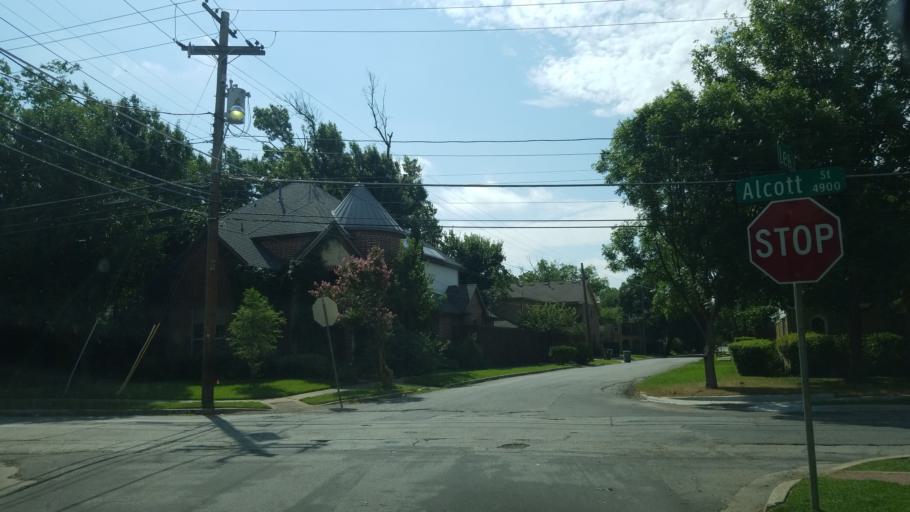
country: US
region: Texas
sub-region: Dallas County
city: Highland Park
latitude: 32.8161
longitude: -96.7858
